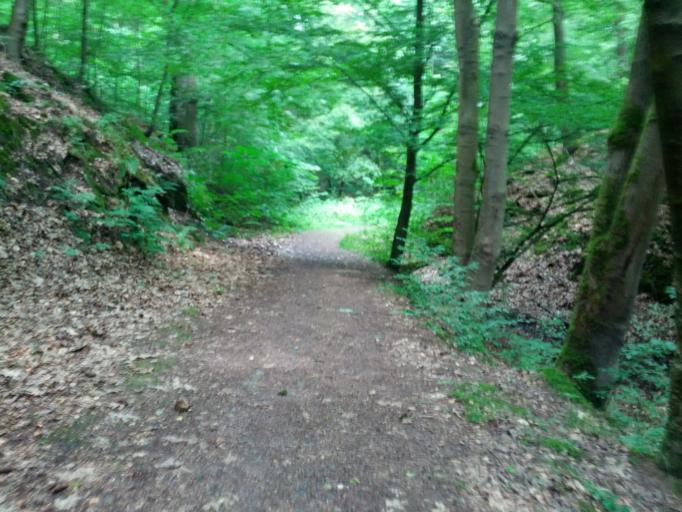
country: DE
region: Thuringia
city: Eisenach
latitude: 50.9607
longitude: 10.3238
